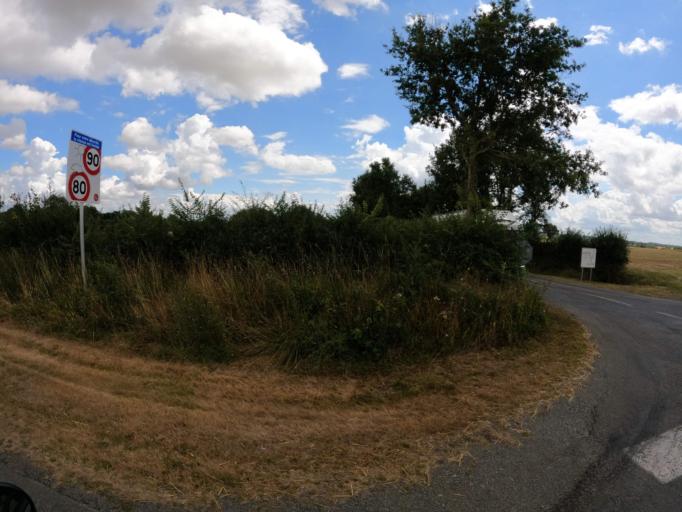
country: FR
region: Pays de la Loire
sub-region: Departement de Maine-et-Loire
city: Mire
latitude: 47.7736
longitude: -0.4741
